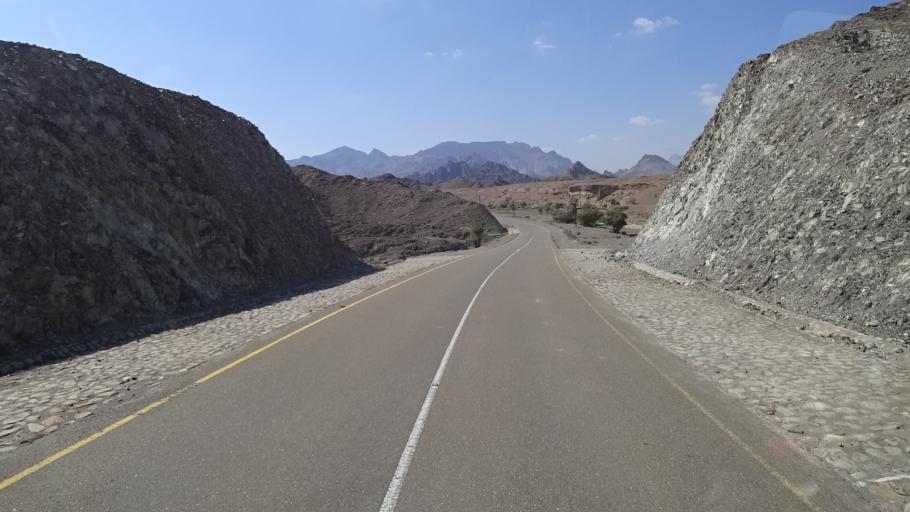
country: OM
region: Al Batinah
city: Al Khaburah
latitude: 23.7513
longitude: 56.9216
